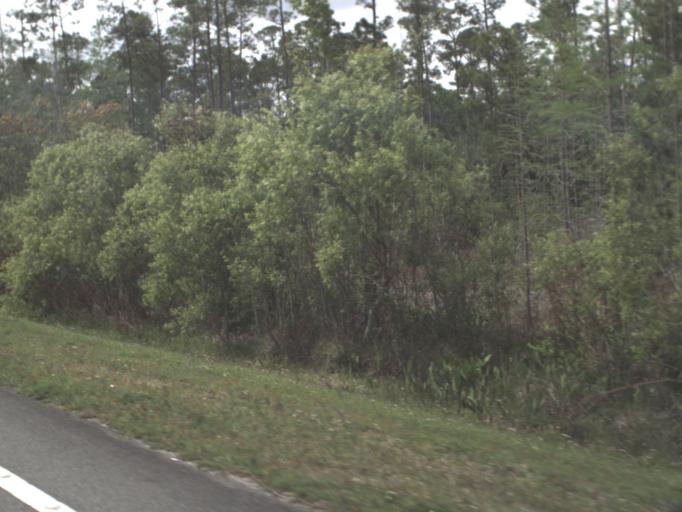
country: US
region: Florida
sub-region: Flagler County
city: Bunnell
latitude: 29.4687
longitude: -81.3141
